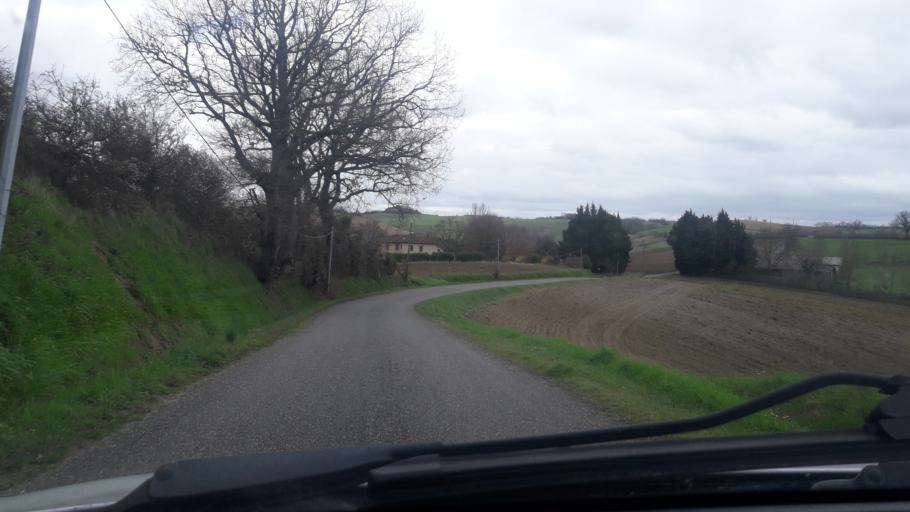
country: FR
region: Midi-Pyrenees
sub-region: Departement de l'Ariege
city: Lezat-sur-Leze
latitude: 43.2130
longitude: 1.3055
